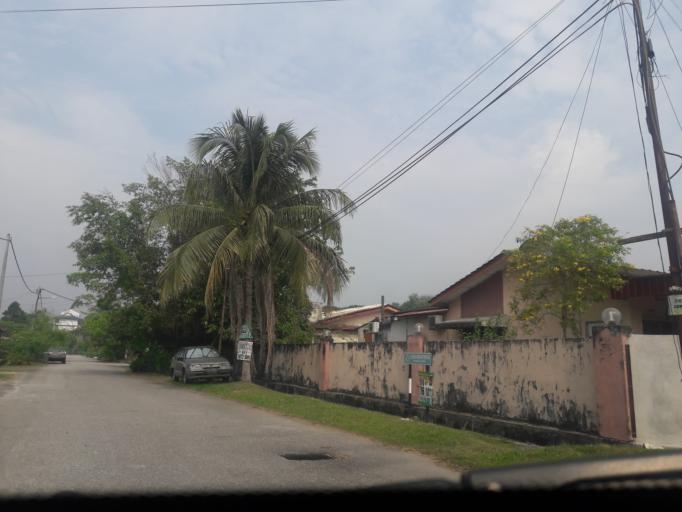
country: MY
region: Kedah
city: Kulim
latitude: 5.3571
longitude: 100.5407
